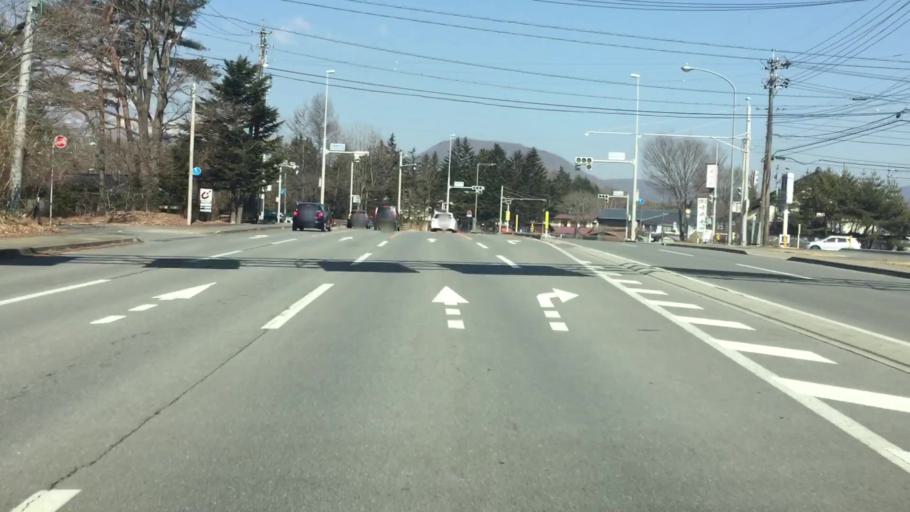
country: JP
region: Nagano
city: Saku
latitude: 36.3234
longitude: 138.6286
